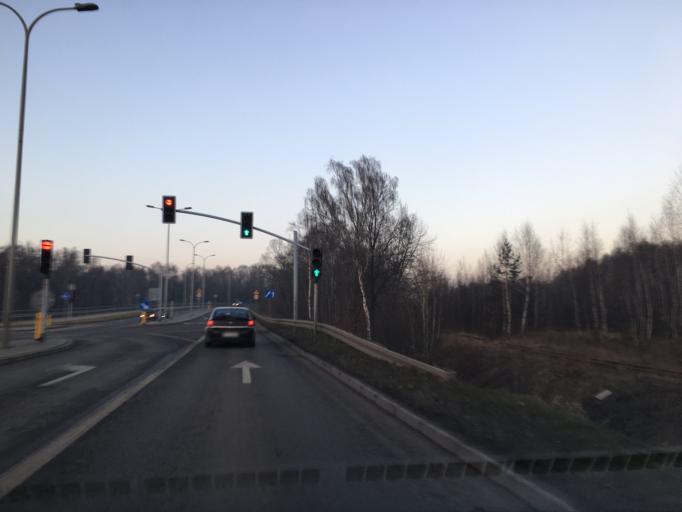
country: PL
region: Silesian Voivodeship
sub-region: Powiat tarnogorski
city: Radzionkow
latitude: 50.3681
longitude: 18.8766
